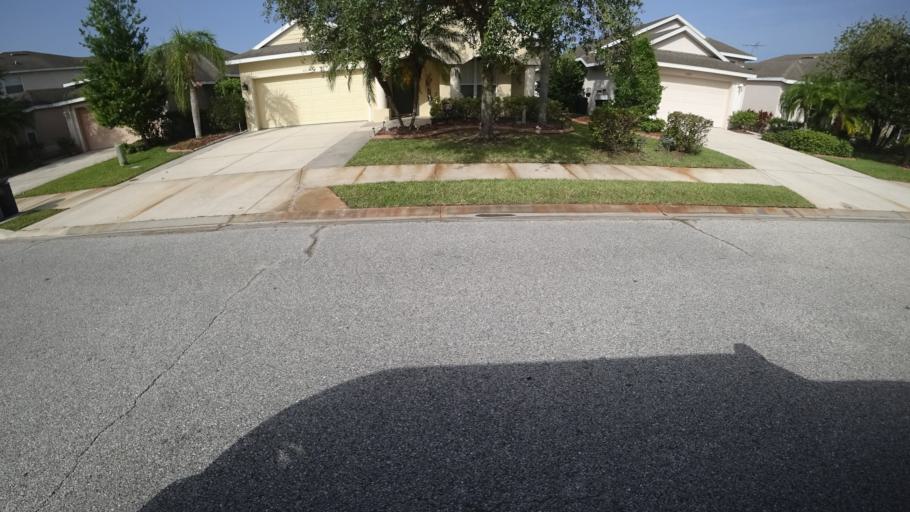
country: US
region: Florida
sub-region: Manatee County
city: Ellenton
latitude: 27.5553
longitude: -82.5002
